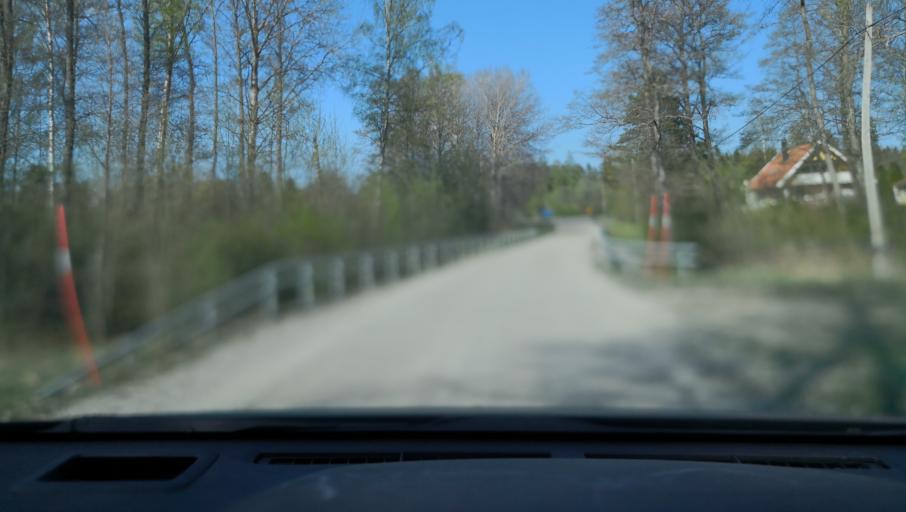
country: SE
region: Uppsala
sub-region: Heby Kommun
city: Heby
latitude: 60.0346
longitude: 16.7829
